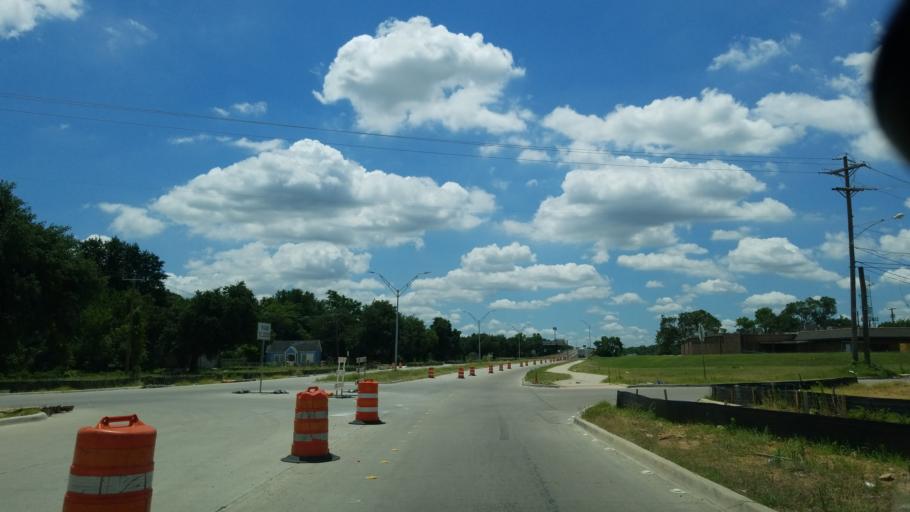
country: US
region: Texas
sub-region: Dallas County
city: Dallas
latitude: 32.7438
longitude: -96.7578
